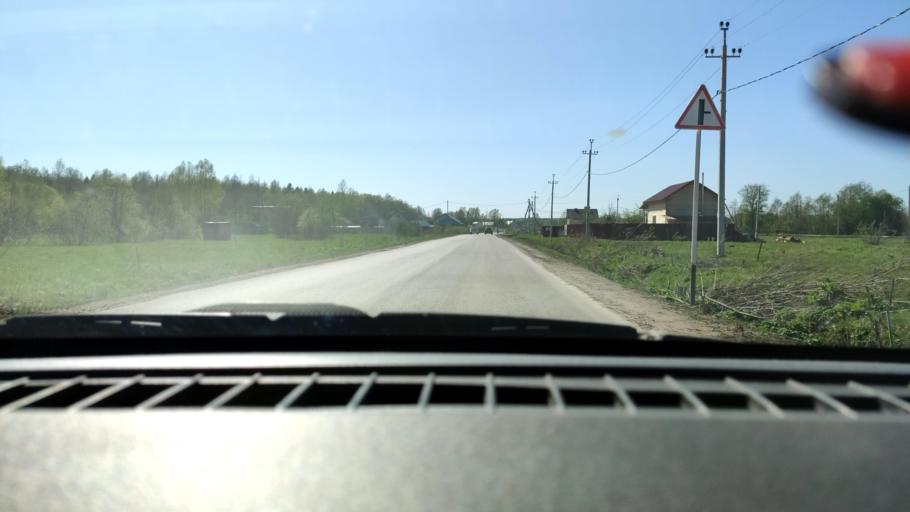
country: RU
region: Perm
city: Overyata
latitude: 58.0790
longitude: 55.9981
